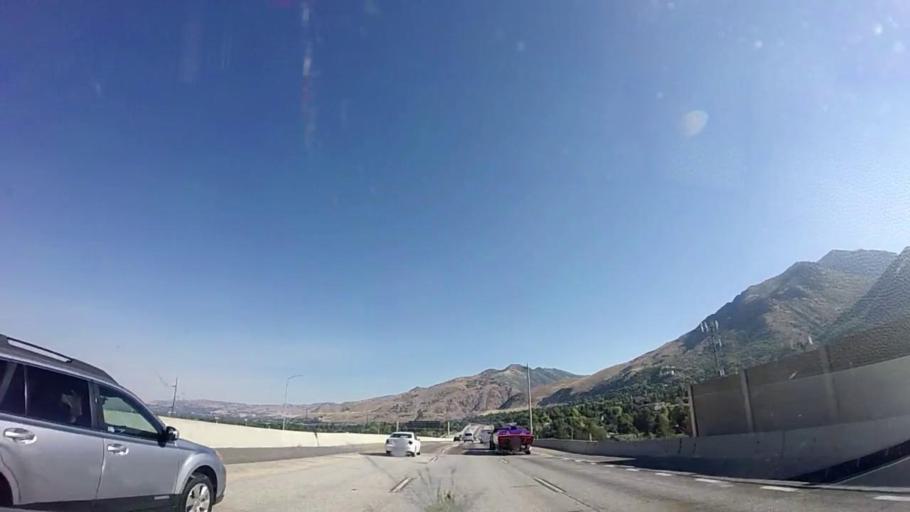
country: US
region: Utah
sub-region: Salt Lake County
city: Mount Olympus
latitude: 40.6882
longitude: -111.7973
